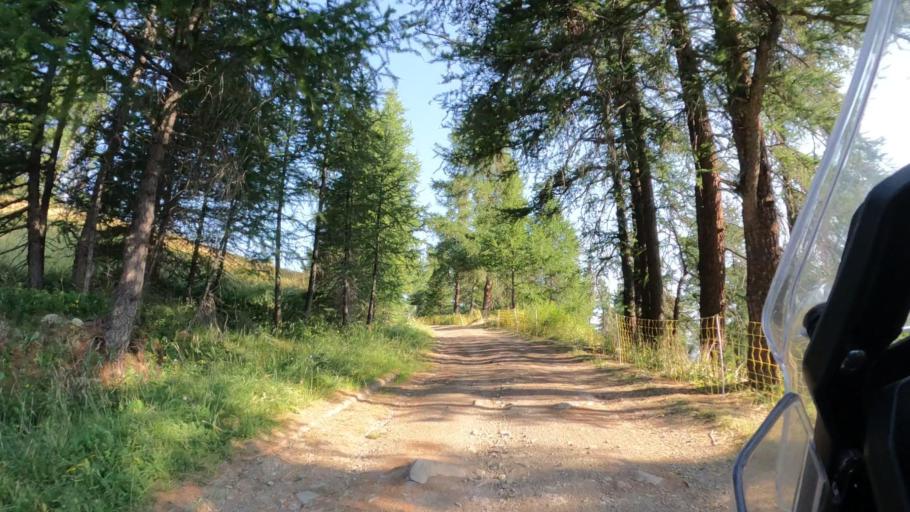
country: FR
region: Provence-Alpes-Cote d'Azur
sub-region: Departement des Hautes-Alpes
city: Guillestre
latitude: 44.6087
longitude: 6.6686
